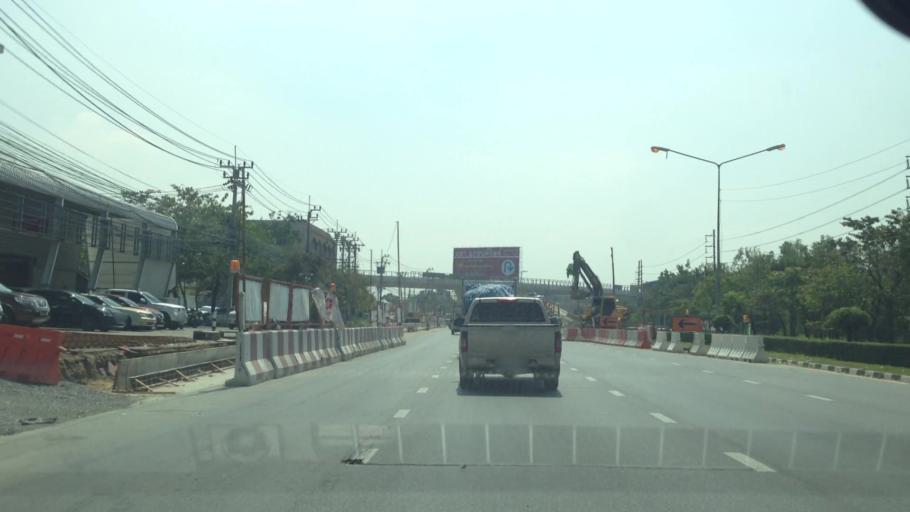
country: TH
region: Bangkok
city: Sai Mai
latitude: 13.9294
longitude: 100.6262
